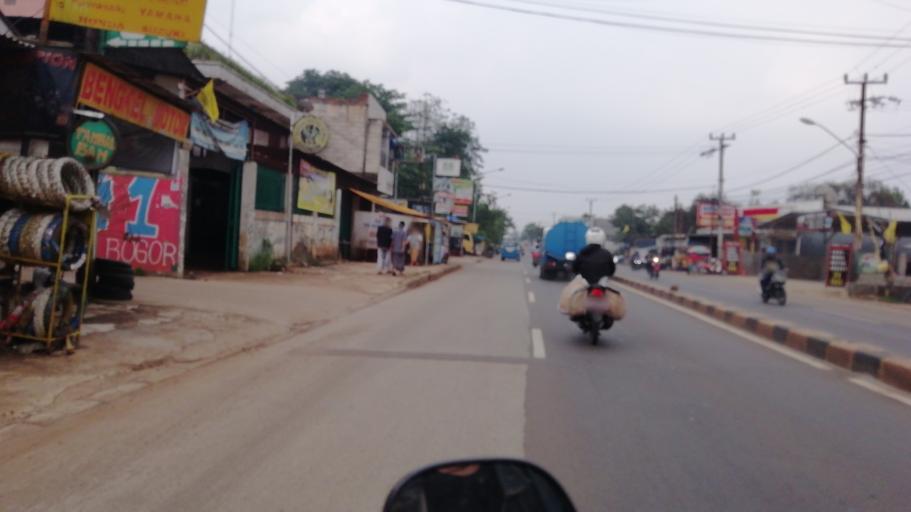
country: ID
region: West Java
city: Parung
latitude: -6.4577
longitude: 106.7307
